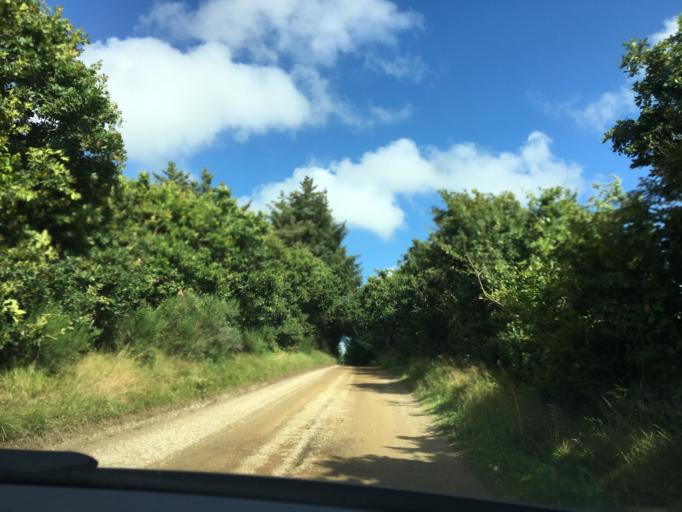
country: DK
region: South Denmark
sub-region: Varde Kommune
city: Oksbol
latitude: 55.7389
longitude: 8.2376
